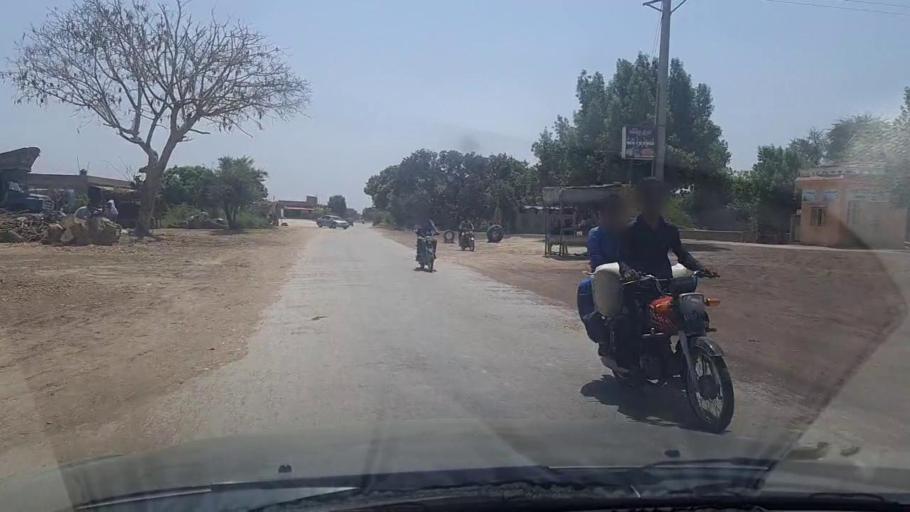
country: PK
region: Sindh
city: Tando Jam
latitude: 25.3009
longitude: 68.5834
